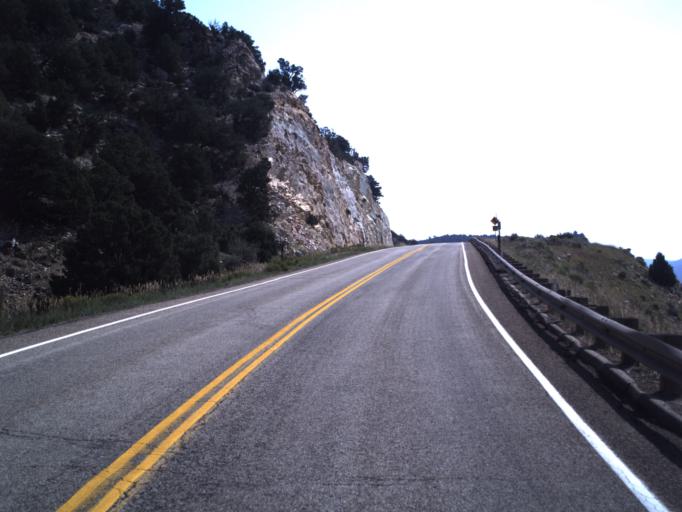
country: US
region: Utah
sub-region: Daggett County
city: Manila
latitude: 40.8950
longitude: -109.7178
